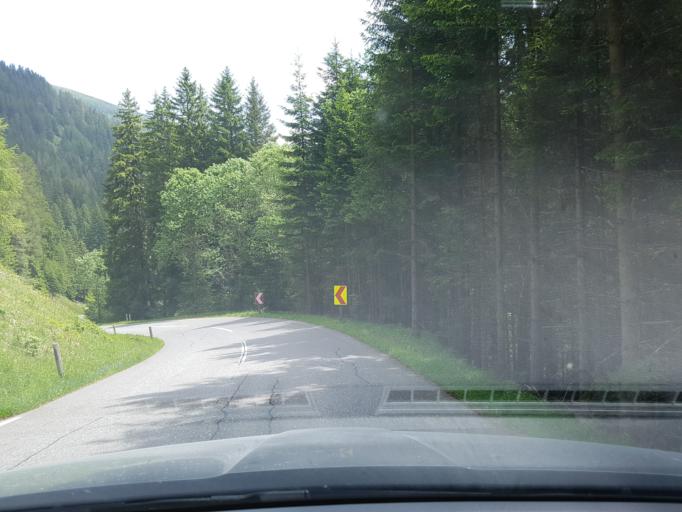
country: AT
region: Carinthia
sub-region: Politischer Bezirk Spittal an der Drau
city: Kleinkirchheim
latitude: 46.8904
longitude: 13.8299
